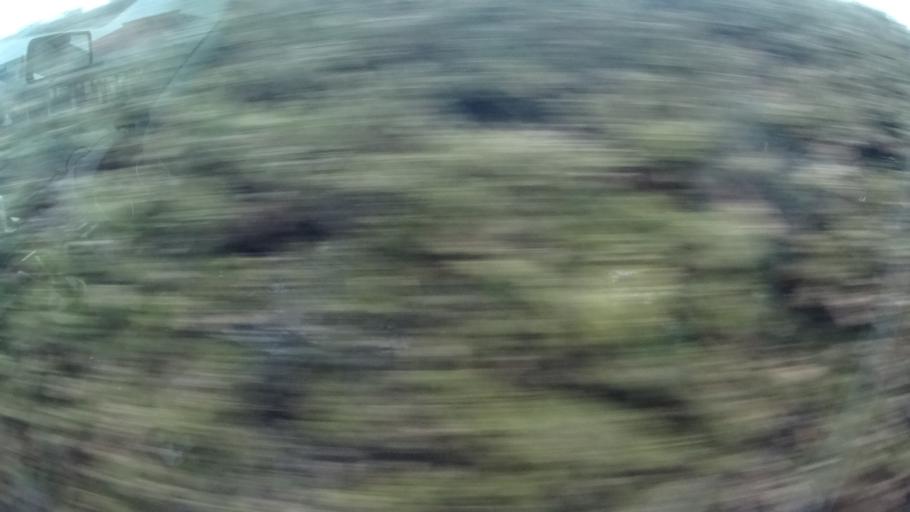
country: DE
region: Bavaria
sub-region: Regierungsbezirk Unterfranken
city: Kitzingen
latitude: 49.7233
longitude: 10.1518
